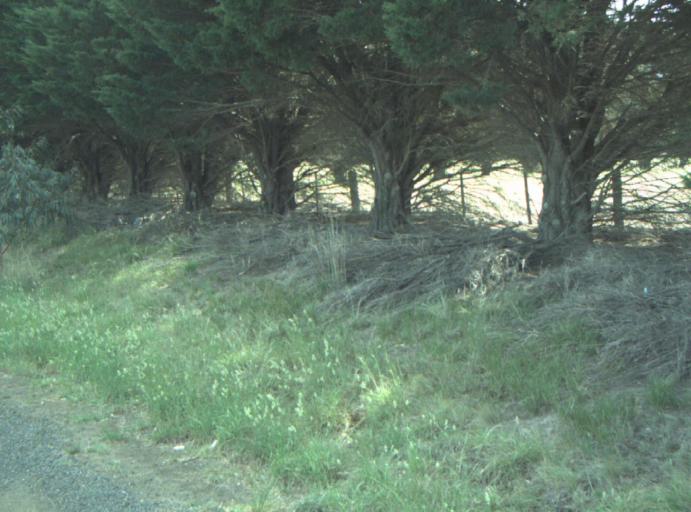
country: AU
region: Victoria
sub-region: Greater Geelong
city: Leopold
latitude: -38.1938
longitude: 144.5105
